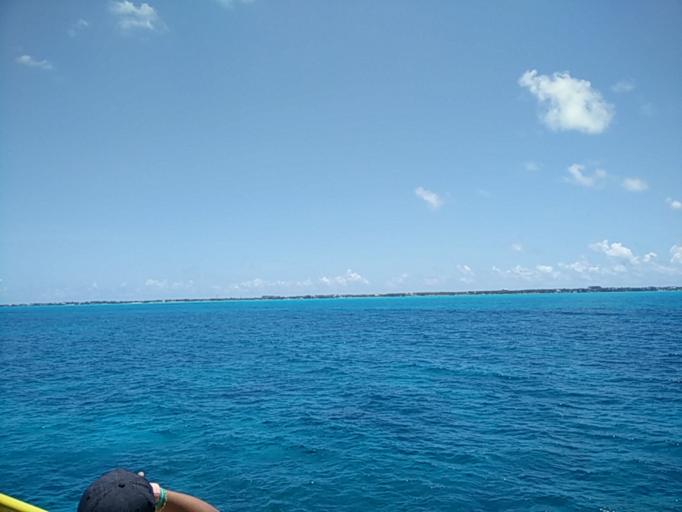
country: MX
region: Quintana Roo
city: Isla Mujeres
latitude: 21.2061
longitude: -86.7594
